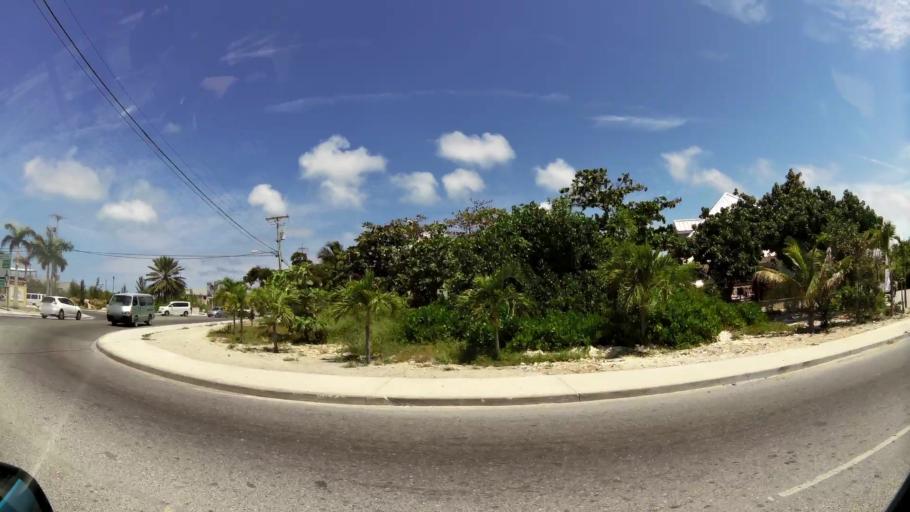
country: BS
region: Mayaguana
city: Abraham's Bay
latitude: 21.7764
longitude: -72.2574
